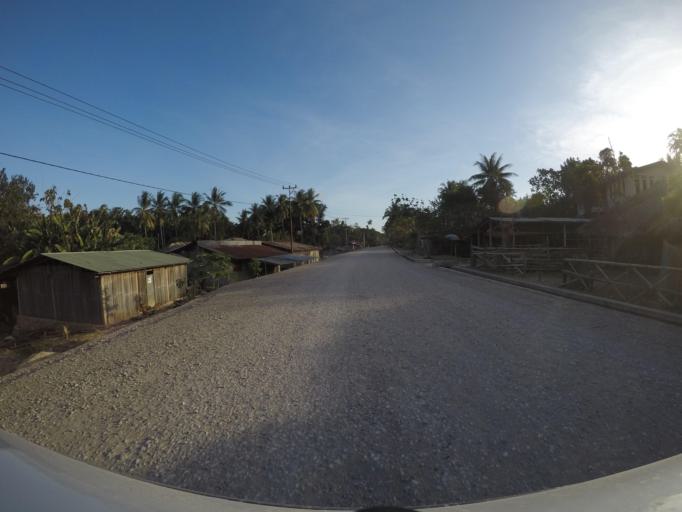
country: TL
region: Viqueque
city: Viqueque
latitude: -8.8369
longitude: 126.5187
